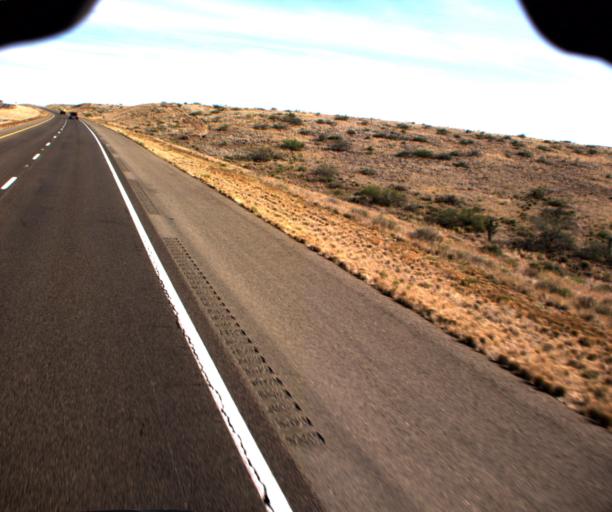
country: US
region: Arizona
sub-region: Cochise County
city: Willcox
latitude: 32.4039
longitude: -109.6617
